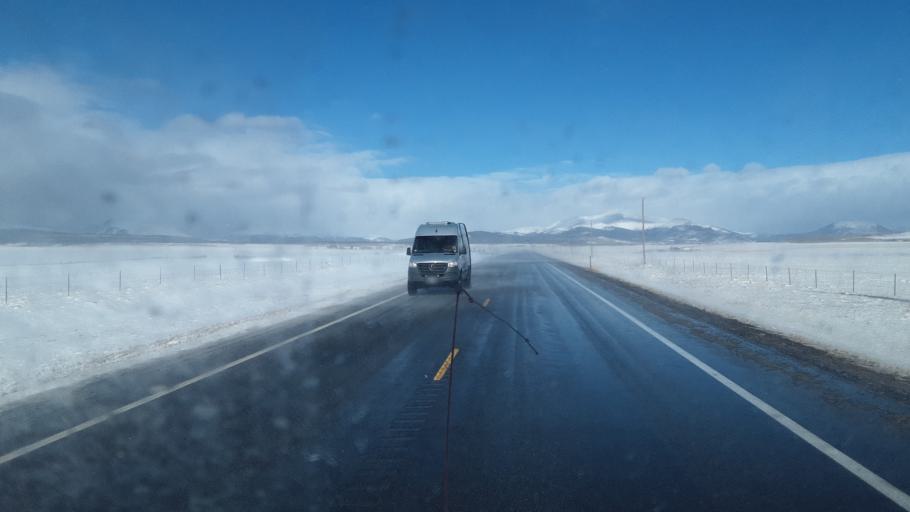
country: US
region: Colorado
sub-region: Park County
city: Fairplay
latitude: 39.1619
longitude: -106.0006
